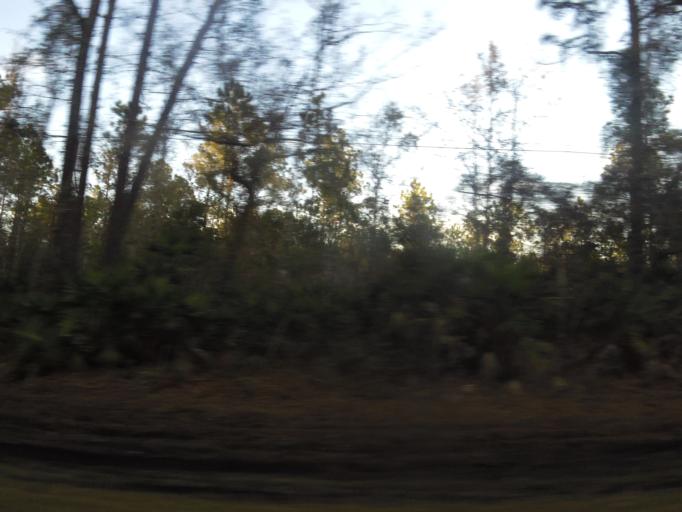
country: US
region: Florida
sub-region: Clay County
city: Green Cove Springs
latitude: 29.8955
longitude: -81.5747
